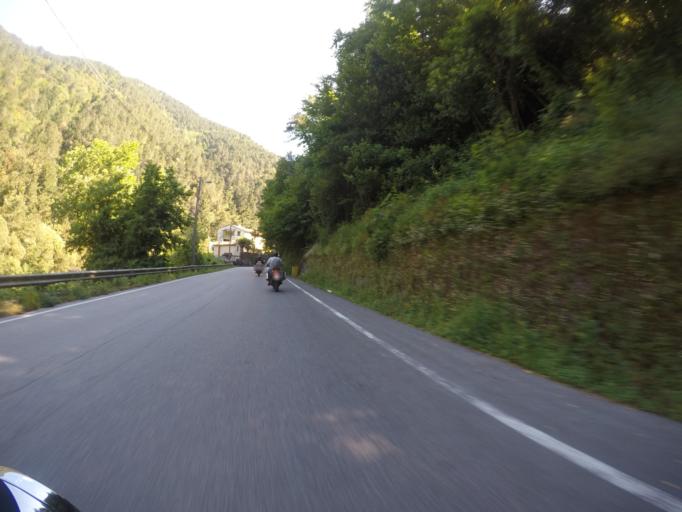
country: IT
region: Tuscany
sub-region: Provincia di Massa-Carrara
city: Montignoso
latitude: 44.0470
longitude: 10.1550
